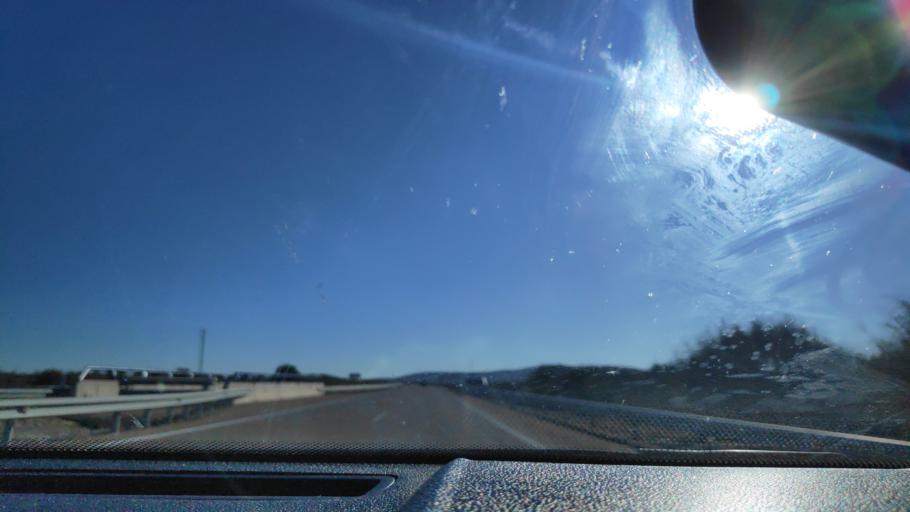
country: ES
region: Extremadura
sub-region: Provincia de Badajoz
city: Villafranca de los Barros
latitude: 38.5517
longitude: -6.3639
